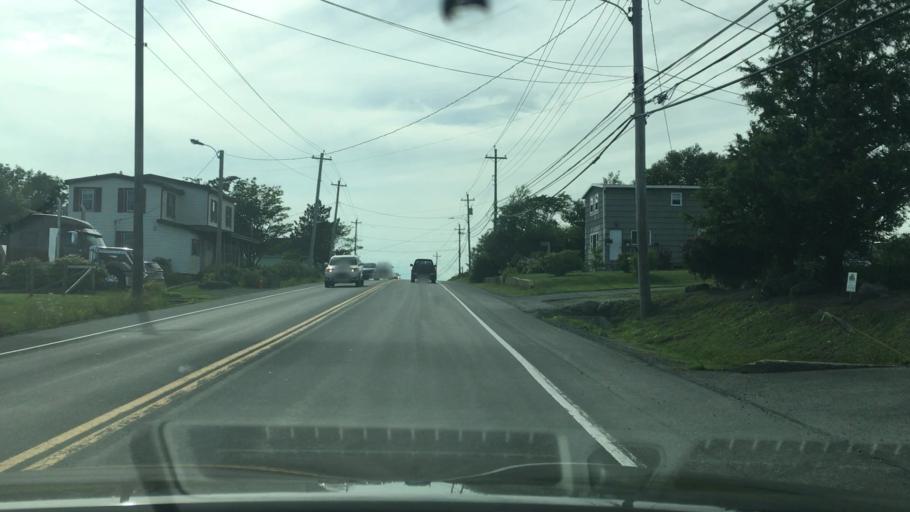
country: CA
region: Nova Scotia
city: Dartmouth
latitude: 44.7336
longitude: -63.7643
